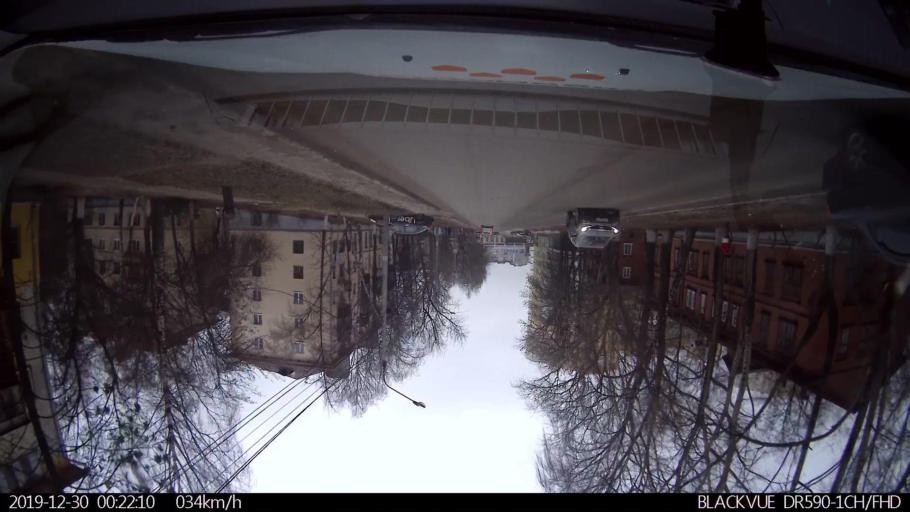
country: RU
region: Nizjnij Novgorod
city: Nizhniy Novgorod
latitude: 56.3122
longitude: 44.0345
